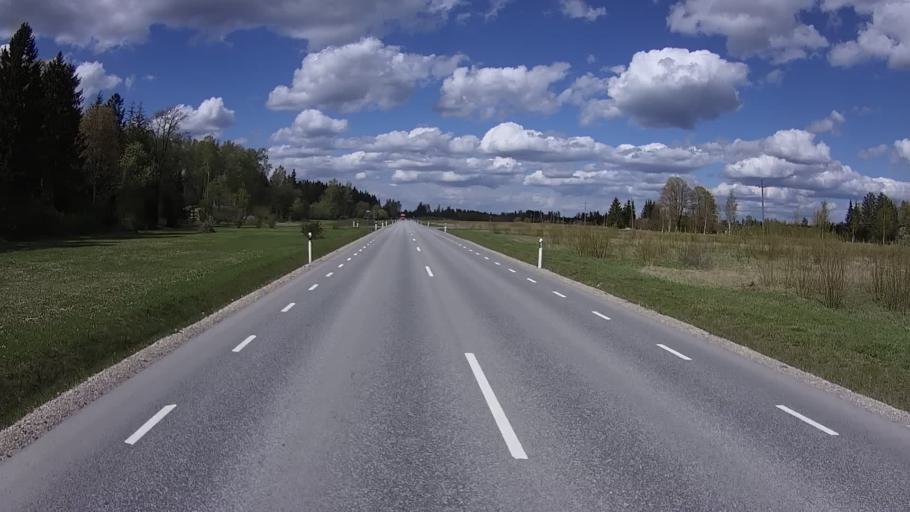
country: EE
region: Jogevamaa
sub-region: Jogeva linn
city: Jogeva
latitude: 58.7648
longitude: 26.3318
